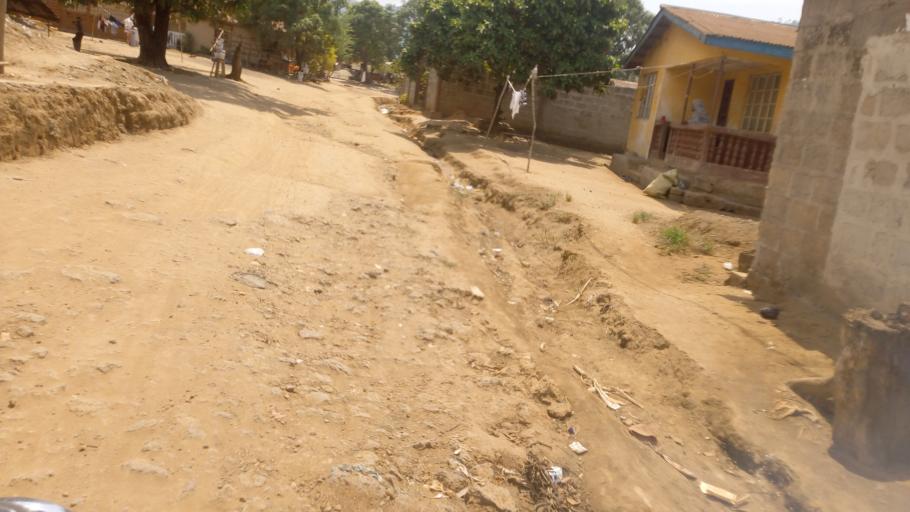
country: SL
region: Western Area
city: Waterloo
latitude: 8.3264
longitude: -13.0751
